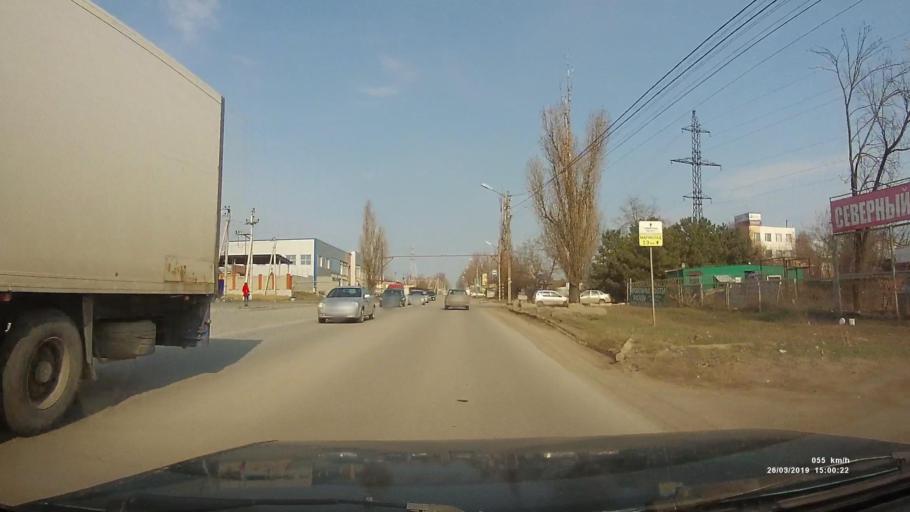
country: RU
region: Rostov
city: Novobessergenovka
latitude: 47.2114
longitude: 38.8690
